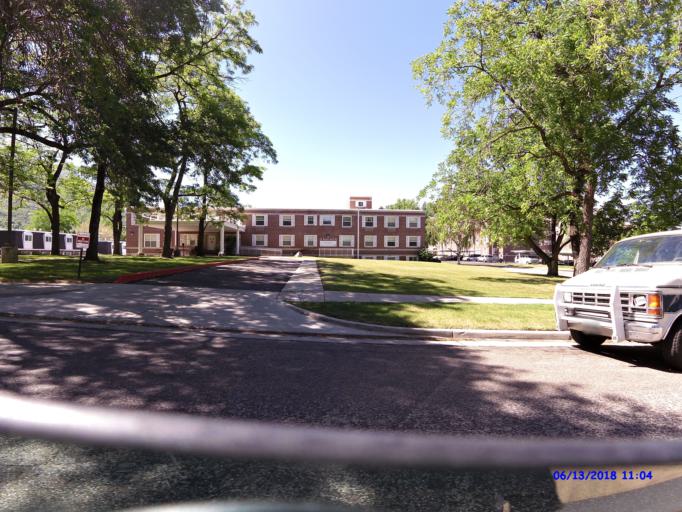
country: US
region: Utah
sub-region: Weber County
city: Ogden
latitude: 41.2109
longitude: -111.9410
